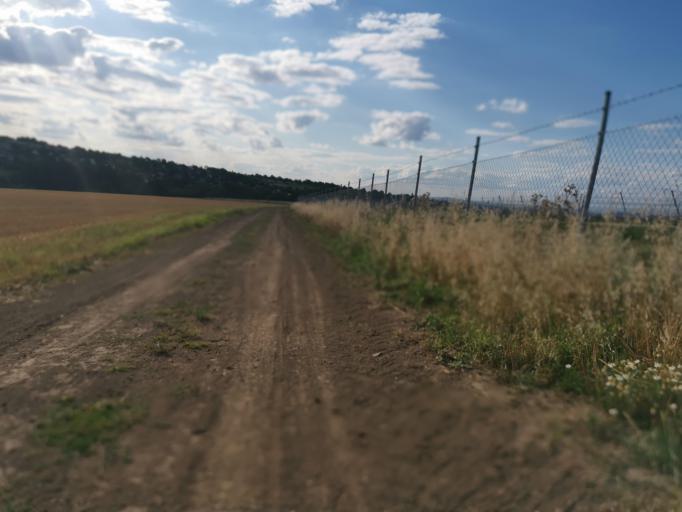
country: SK
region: Trnavsky
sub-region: Okres Skalica
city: Skalica
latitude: 48.8249
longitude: 17.2571
